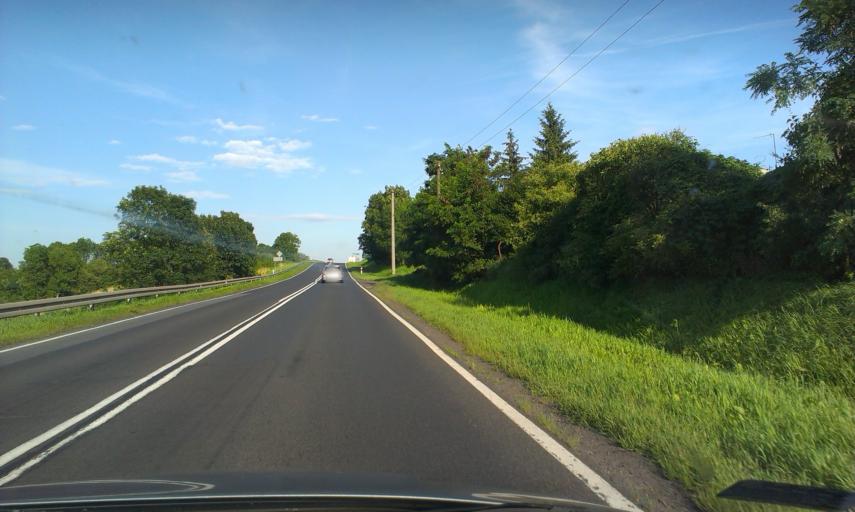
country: PL
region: Kujawsko-Pomorskie
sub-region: Powiat bydgoski
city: Sicienko
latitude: 53.1667
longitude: 17.7782
